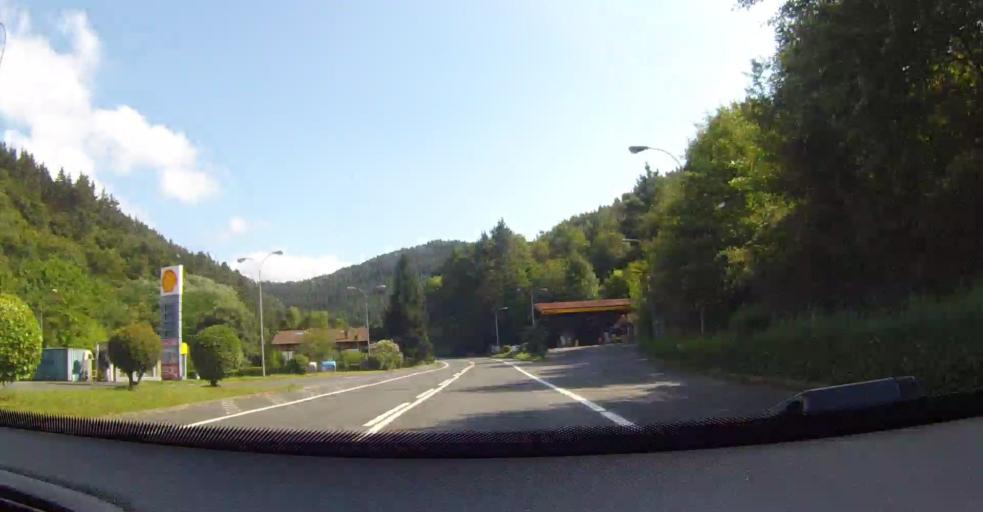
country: ES
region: Basque Country
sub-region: Bizkaia
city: Muxika
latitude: 43.2662
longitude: -2.6861
